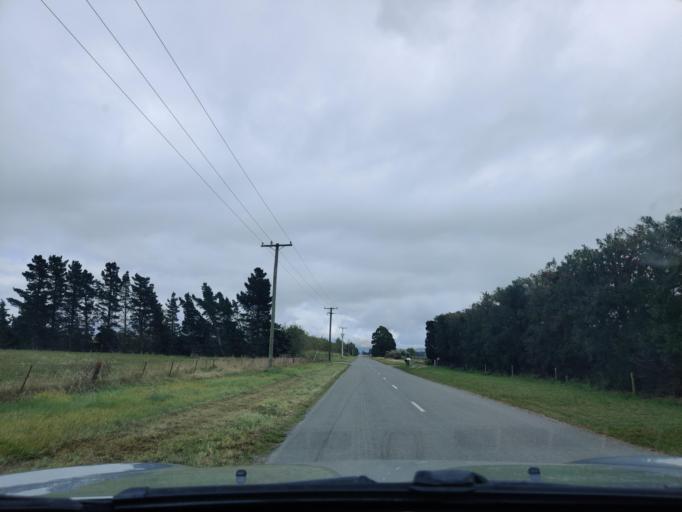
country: NZ
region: Canterbury
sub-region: Hurunui District
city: Amberley
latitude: -43.0768
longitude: 172.7138
